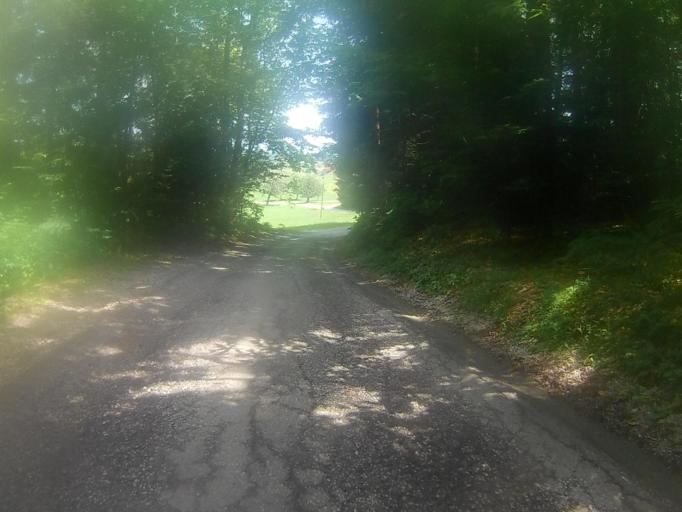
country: SI
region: Maribor
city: Bresternica
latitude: 46.6153
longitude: 15.5627
